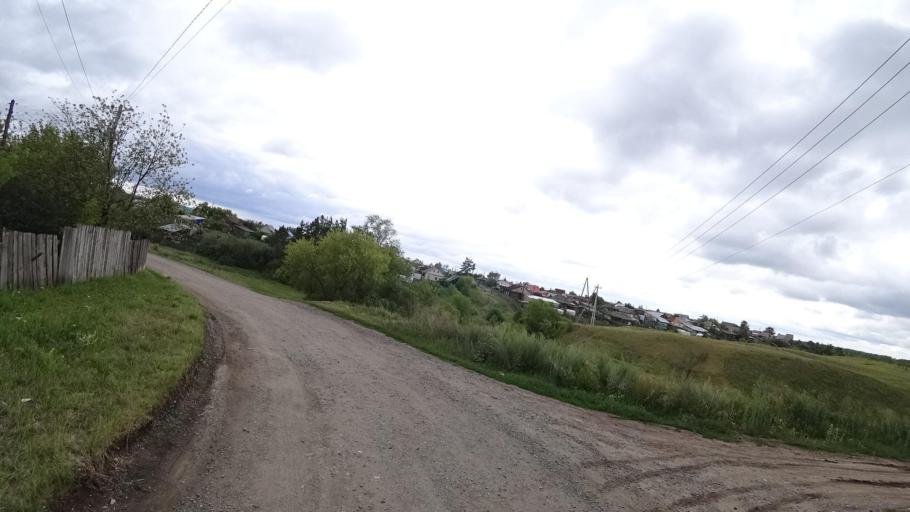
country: RU
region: Sverdlovsk
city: Kamyshlov
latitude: 56.8511
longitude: 62.6828
